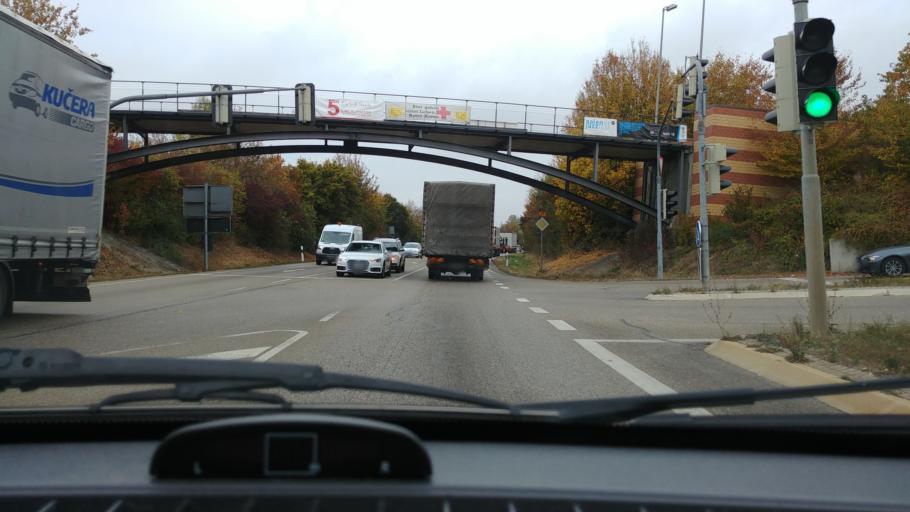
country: DE
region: Baden-Wuerttemberg
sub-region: Regierungsbezirk Stuttgart
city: Aalen
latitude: 48.8384
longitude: 10.0655
